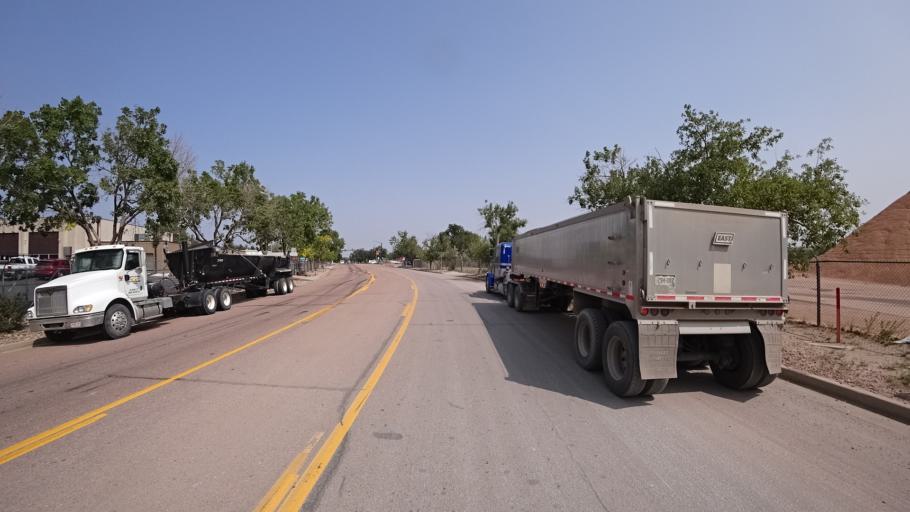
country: US
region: Colorado
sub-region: El Paso County
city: Stratmoor
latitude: 38.7929
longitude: -104.7696
